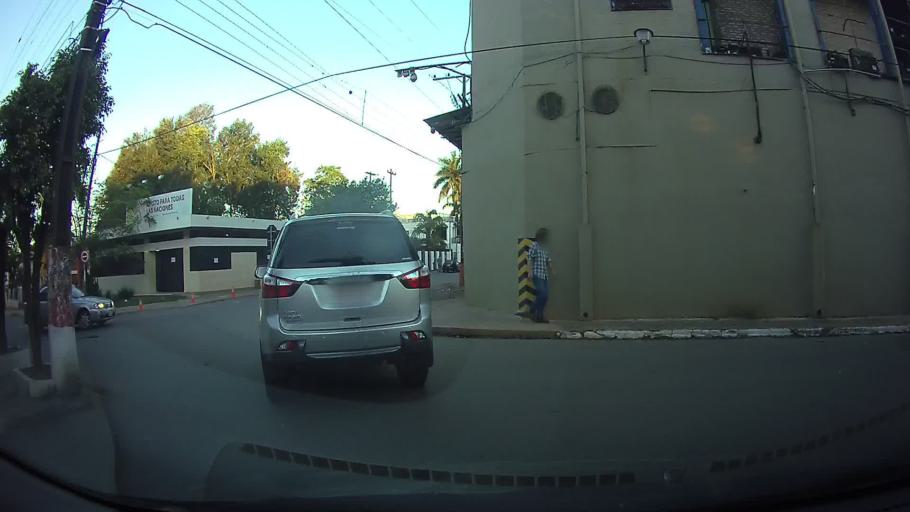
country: PY
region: Central
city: Fernando de la Mora
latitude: -25.3233
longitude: -57.5520
